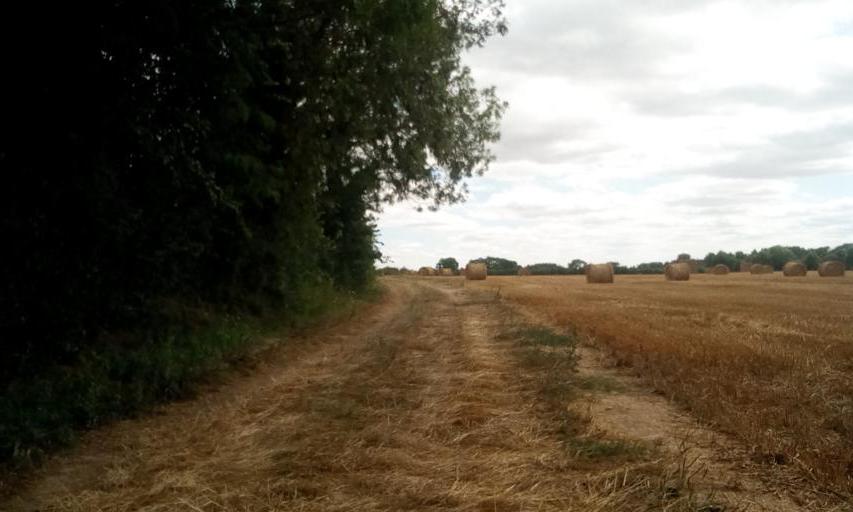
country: FR
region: Lower Normandy
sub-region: Departement du Calvados
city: Troarn
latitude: 49.1677
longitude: -0.1924
